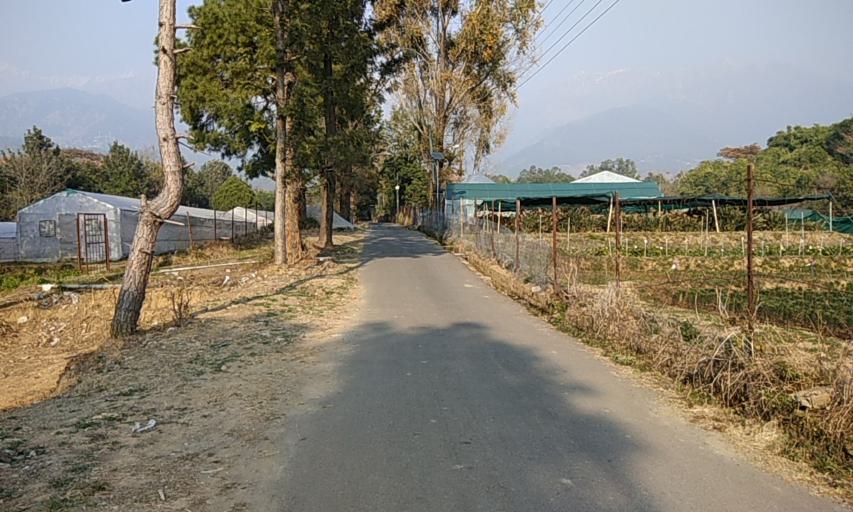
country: IN
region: Himachal Pradesh
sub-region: Kangra
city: Palampur
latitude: 32.1064
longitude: 76.5574
